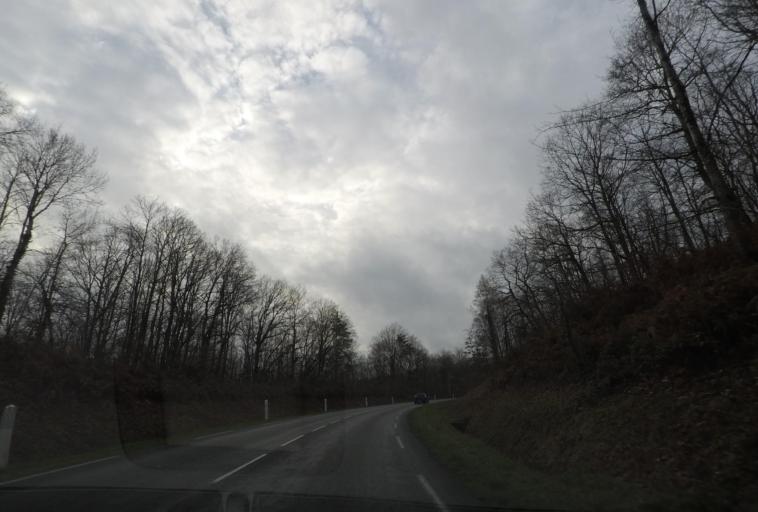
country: FR
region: Pays de la Loire
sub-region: Departement de la Sarthe
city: Vibraye
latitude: 48.0436
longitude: 0.7463
